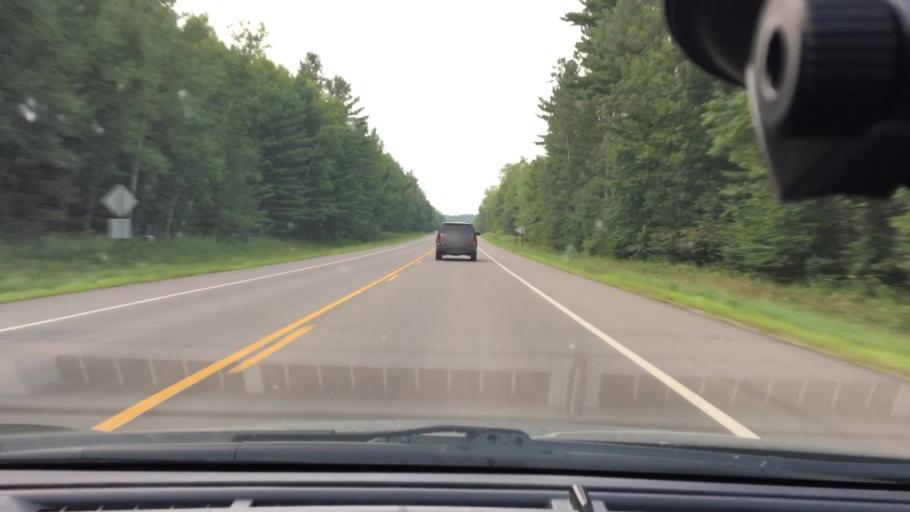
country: US
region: Minnesota
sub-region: Crow Wing County
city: Crosby
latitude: 46.4914
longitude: -93.9366
